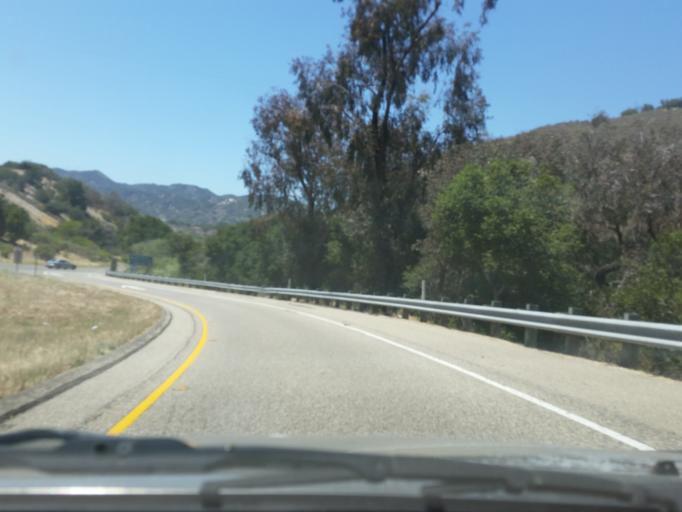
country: US
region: California
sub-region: San Luis Obispo County
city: Avila Beach
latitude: 35.1793
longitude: -120.6979
